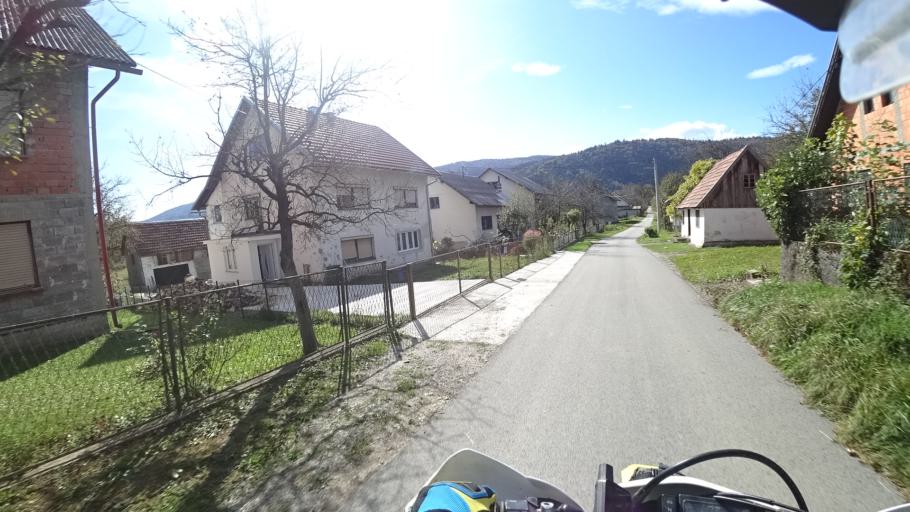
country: HR
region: Karlovacka
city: Plaski
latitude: 45.0797
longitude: 15.3577
